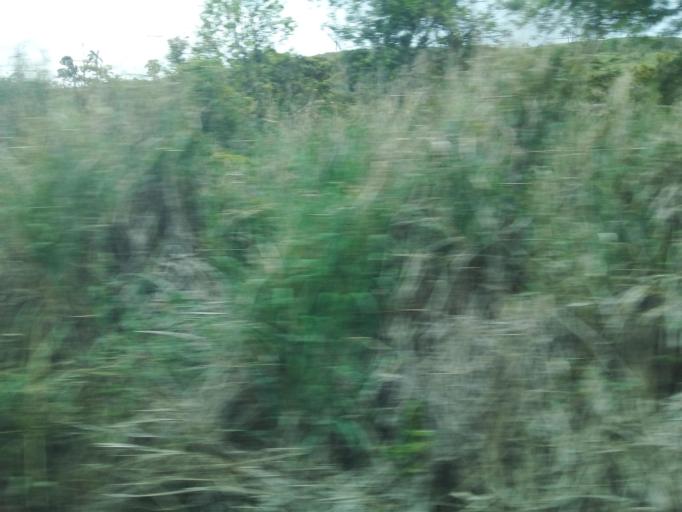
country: BR
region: Minas Gerais
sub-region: Rio Piracicaba
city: Rio Piracicaba
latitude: -19.9731
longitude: -43.2189
